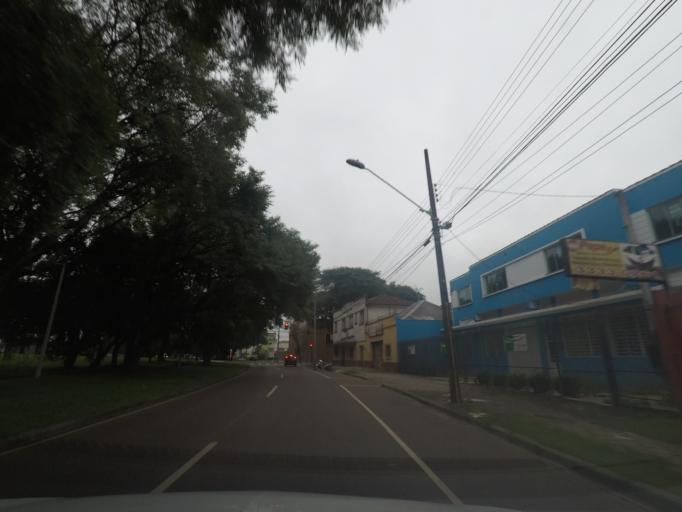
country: BR
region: Parana
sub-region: Curitiba
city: Curitiba
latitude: -25.4510
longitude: -49.2571
